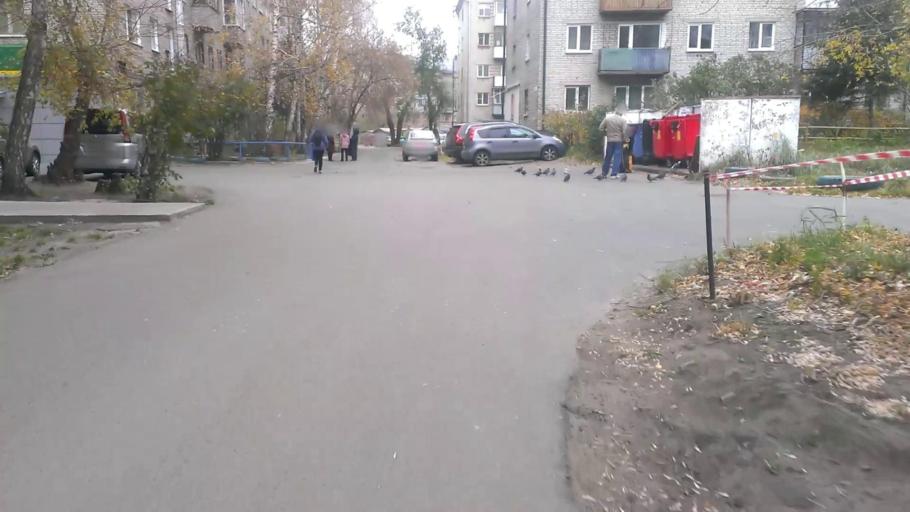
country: RU
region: Altai Krai
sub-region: Gorod Barnaulskiy
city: Barnaul
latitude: 53.3541
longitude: 83.7756
